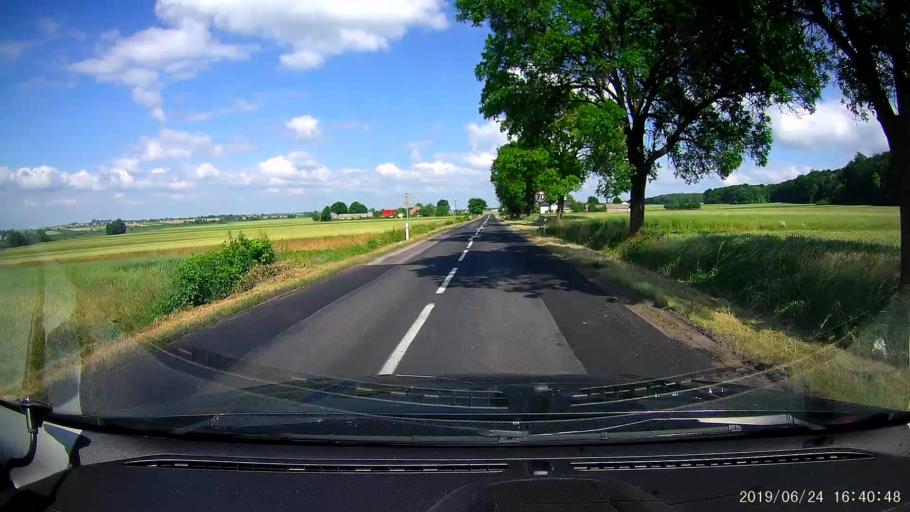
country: PL
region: Lublin Voivodeship
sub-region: Powiat tomaszowski
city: Michalow
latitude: 50.5308
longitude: 23.5823
